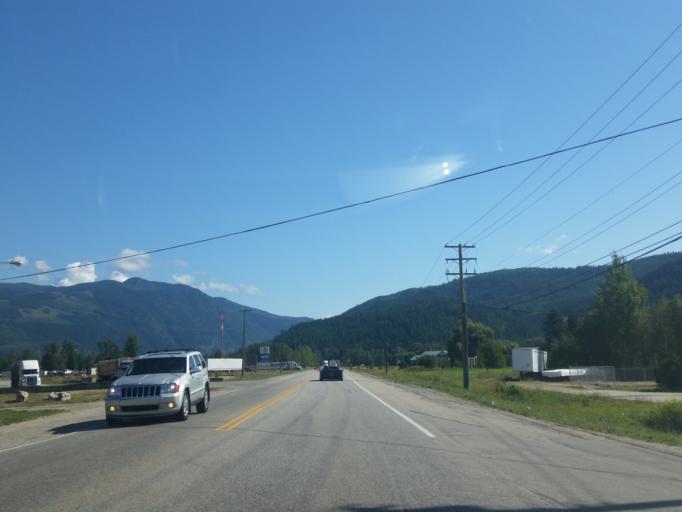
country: CA
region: British Columbia
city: Sicamous
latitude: 50.8429
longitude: -118.9584
